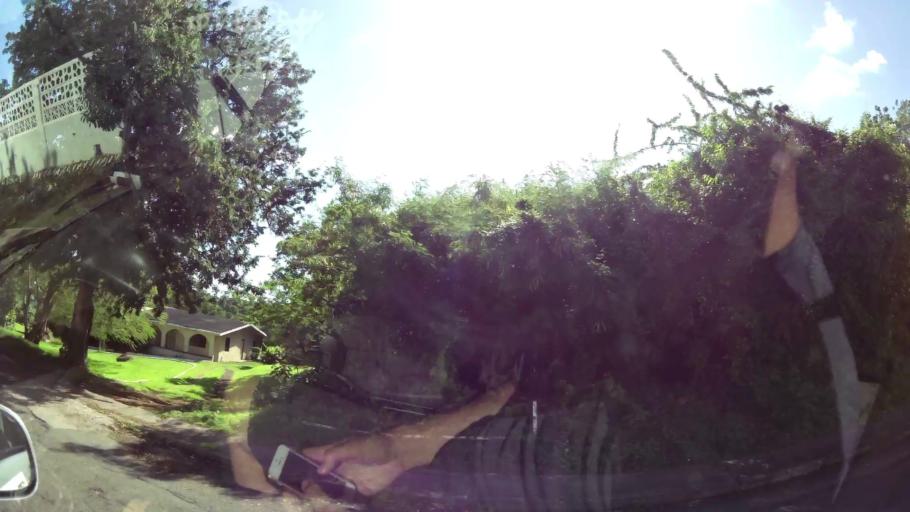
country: GD
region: Saint George
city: Saint George's
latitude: 12.0060
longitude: -61.7671
